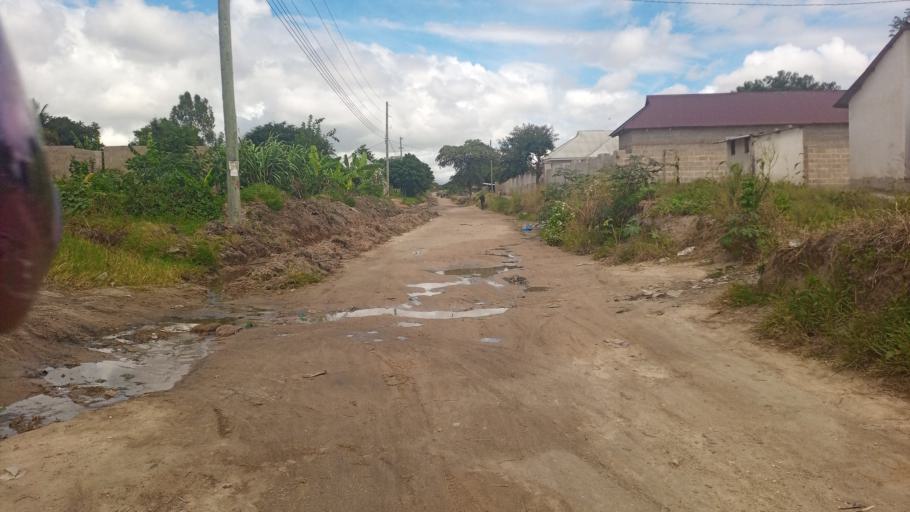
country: TZ
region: Dodoma
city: Dodoma
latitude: -6.1886
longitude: 35.7246
